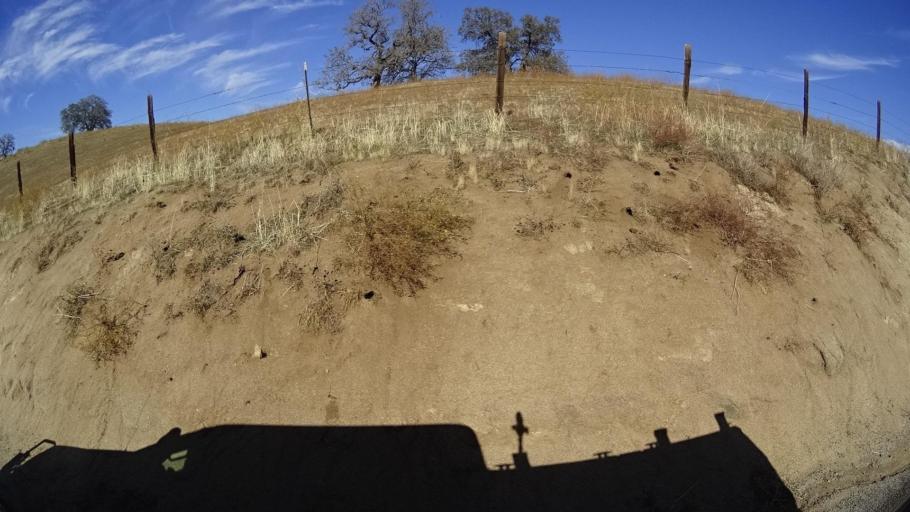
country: US
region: California
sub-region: Tulare County
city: Richgrove
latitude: 35.6928
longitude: -118.8685
